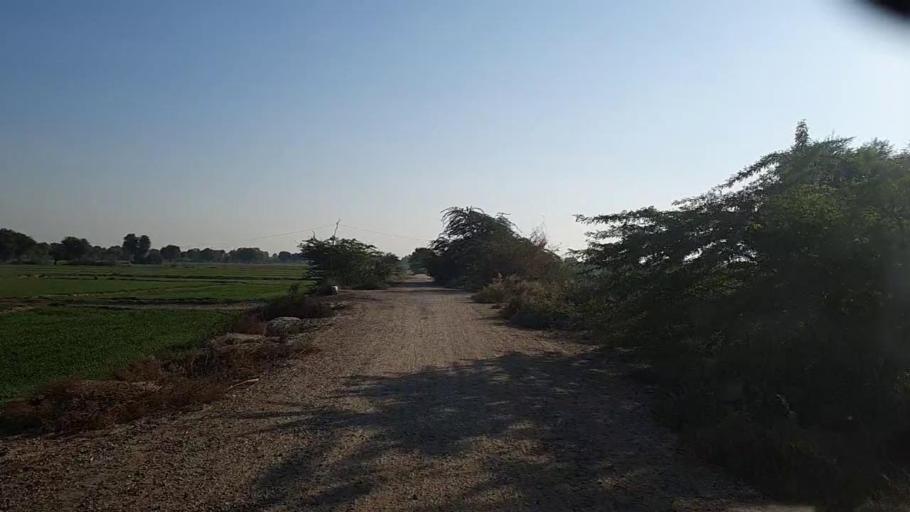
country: PK
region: Sindh
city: Darya Khan Marri
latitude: 26.6895
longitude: 68.3625
